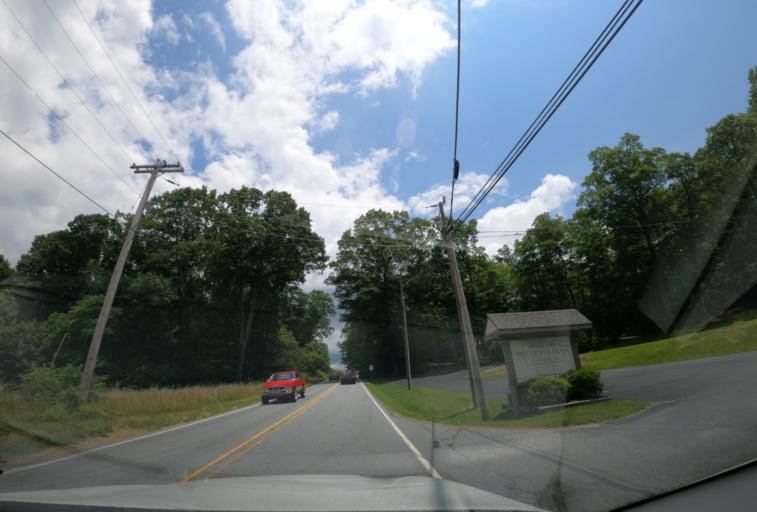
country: US
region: North Carolina
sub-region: Jackson County
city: Cullowhee
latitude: 35.1130
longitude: -83.1114
